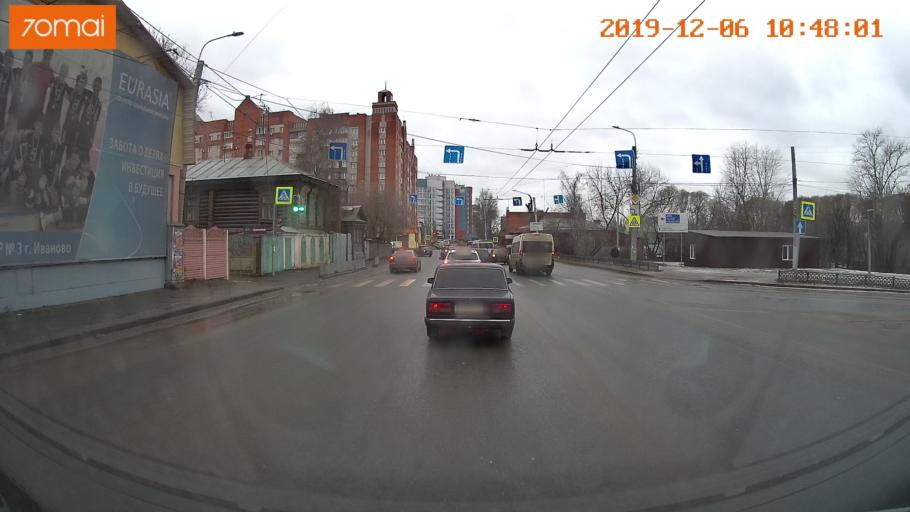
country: RU
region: Ivanovo
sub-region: Gorod Ivanovo
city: Ivanovo
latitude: 56.9965
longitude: 40.9698
